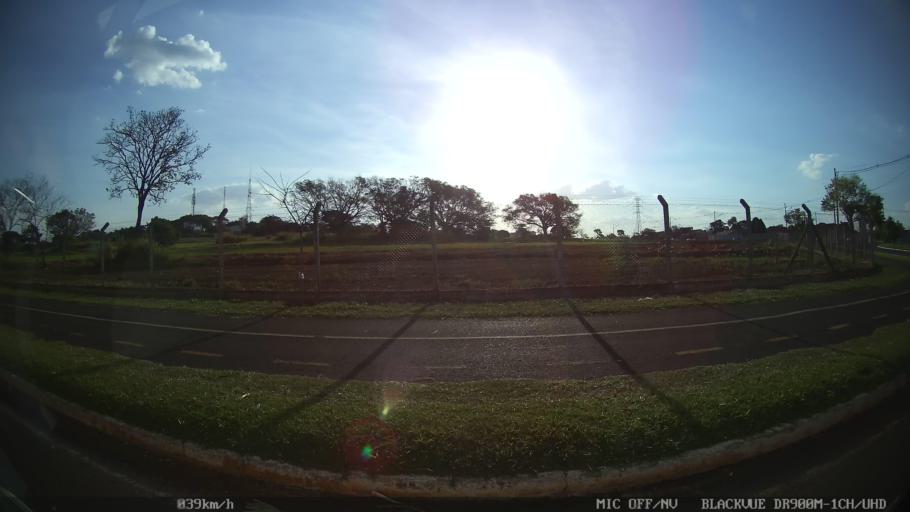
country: BR
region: Sao Paulo
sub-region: Ribeirao Preto
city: Ribeirao Preto
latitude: -21.1613
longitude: -47.8423
